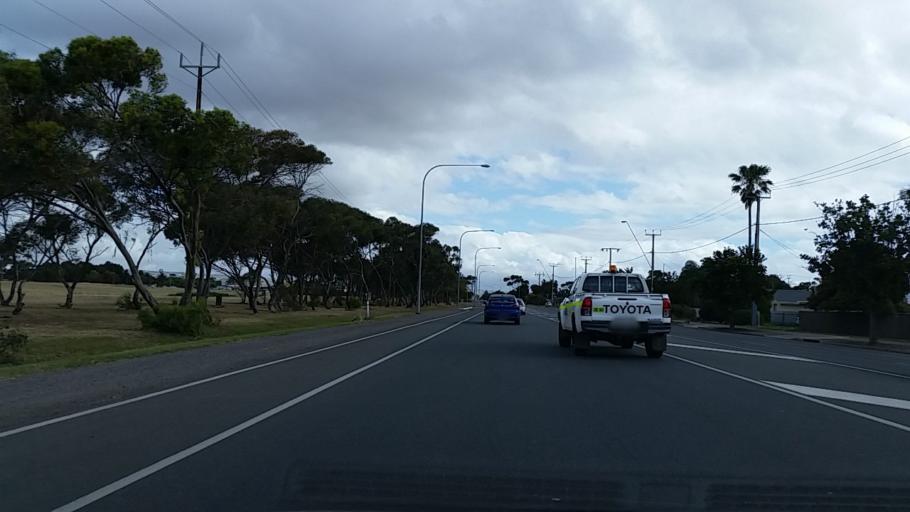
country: AU
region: South Australia
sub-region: Onkaparinga
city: Seaford
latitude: -35.1823
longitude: 138.4769
